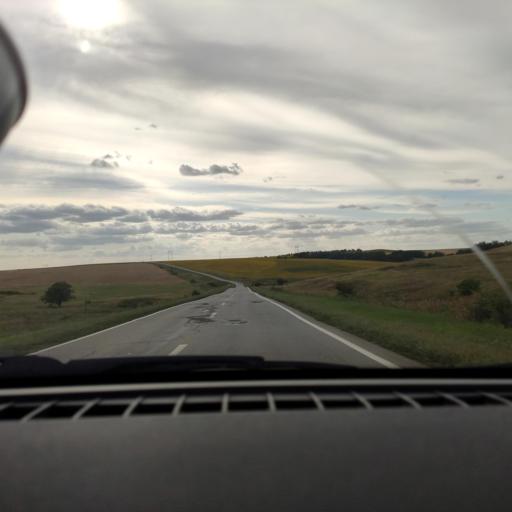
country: RU
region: Samara
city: Kinel'
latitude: 53.4420
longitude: 50.6171
